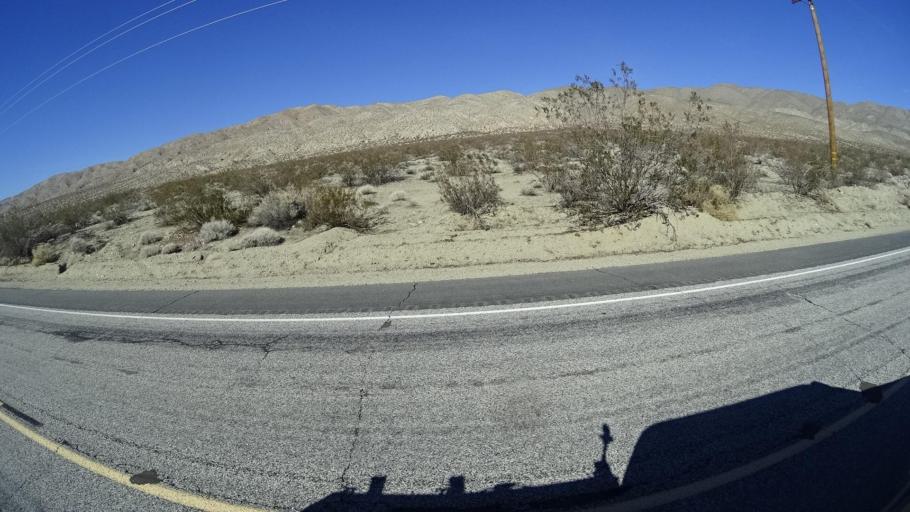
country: US
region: California
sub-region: Kern County
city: California City
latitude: 35.3723
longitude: -117.8756
